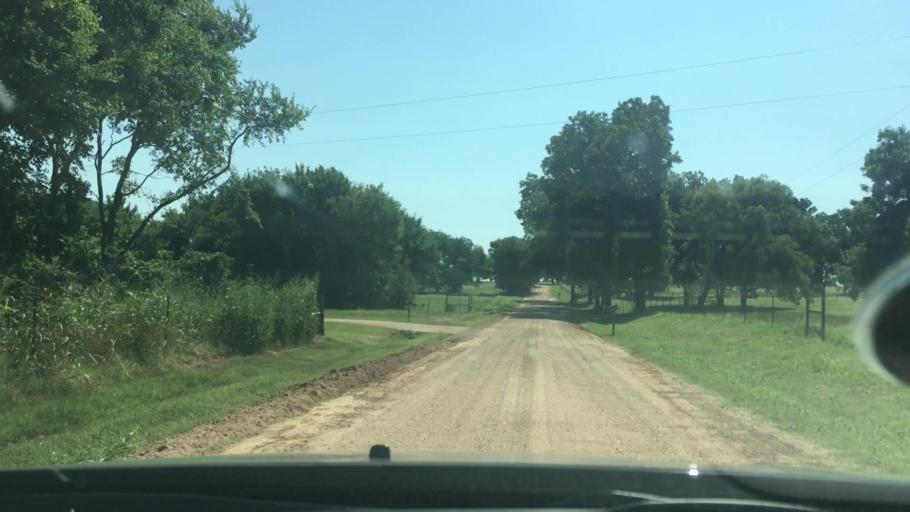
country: US
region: Oklahoma
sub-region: Johnston County
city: Tishomingo
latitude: 34.3104
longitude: -96.6105
